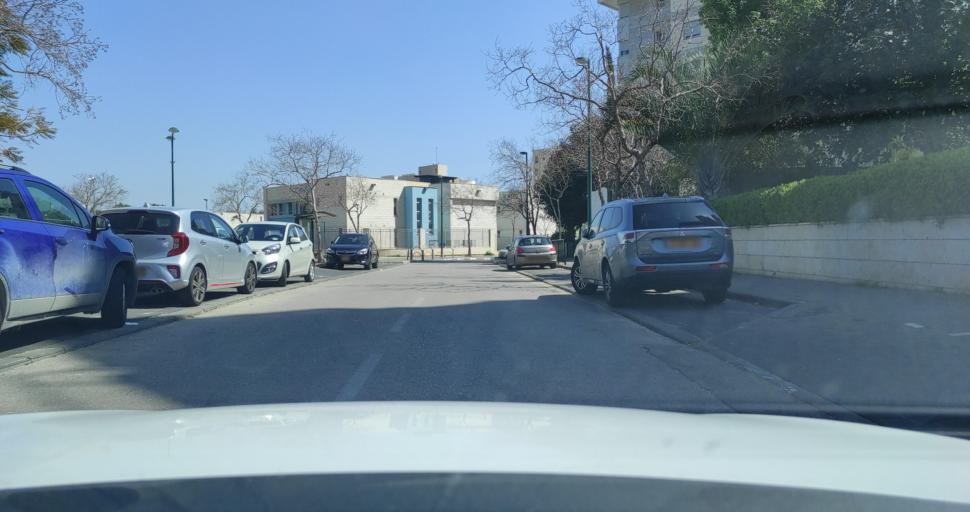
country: IL
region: Central District
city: Nordiyya
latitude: 32.2987
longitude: 34.8754
